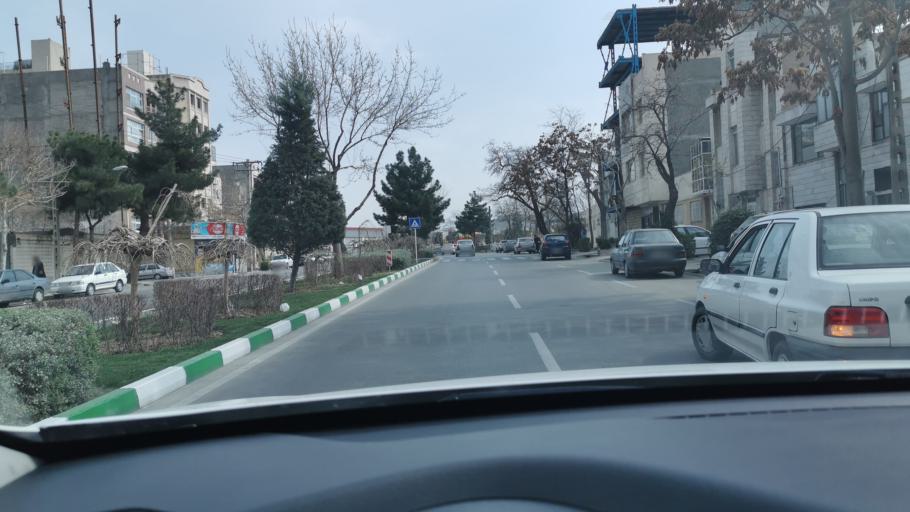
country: IR
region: Razavi Khorasan
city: Mashhad
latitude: 36.2755
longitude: 59.5668
